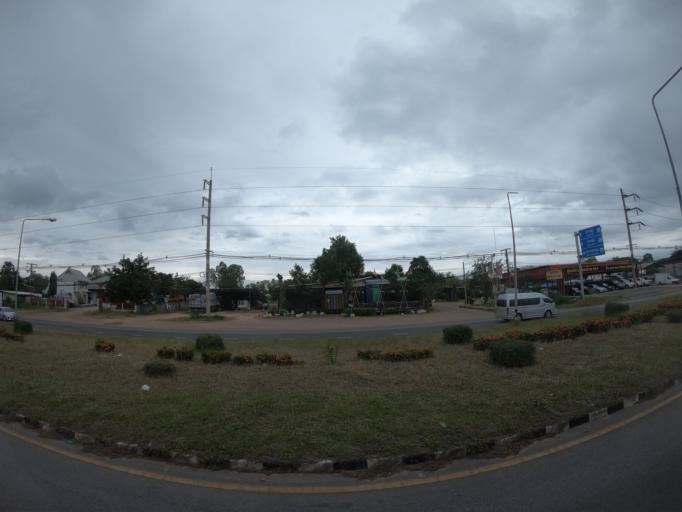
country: TH
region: Roi Et
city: Roi Et
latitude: 16.0434
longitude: 103.6307
